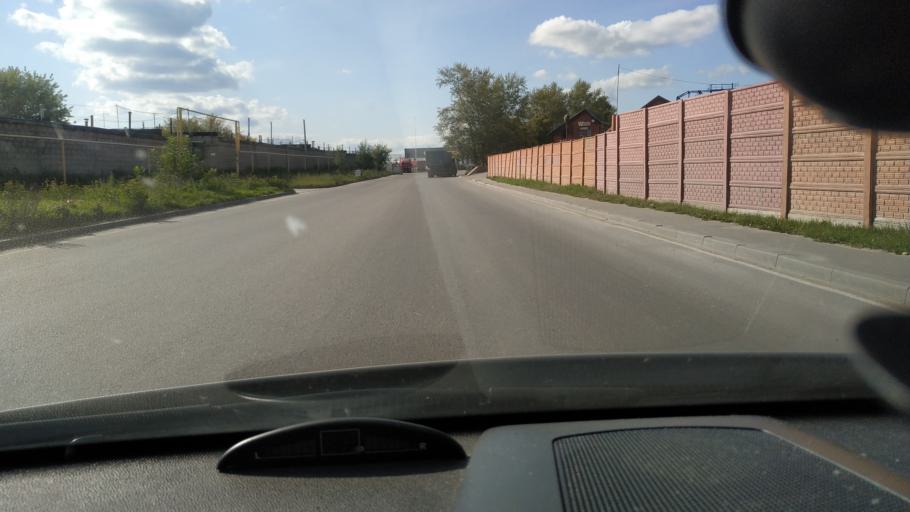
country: RU
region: Rjazan
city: Ryazan'
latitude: 54.6527
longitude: 39.6432
